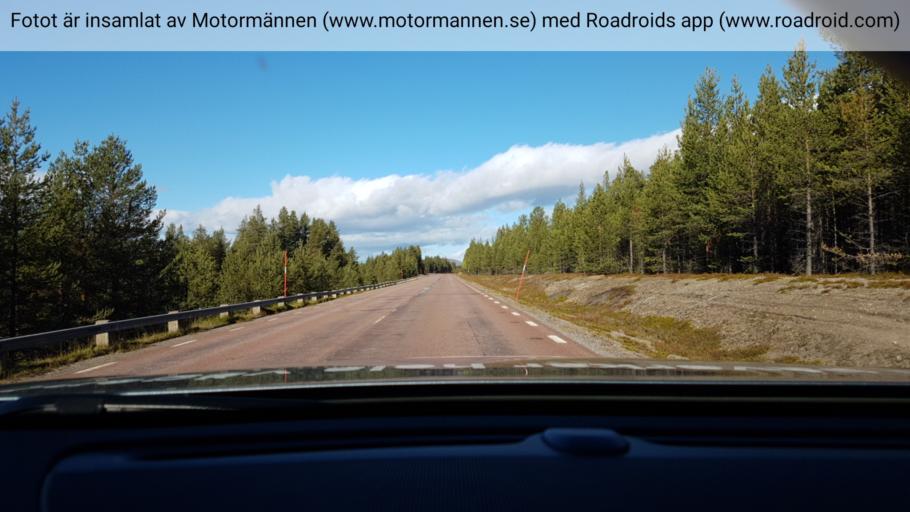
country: SE
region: Norrbotten
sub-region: Arjeplogs Kommun
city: Arjeplog
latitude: 66.0242
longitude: 18.0680
